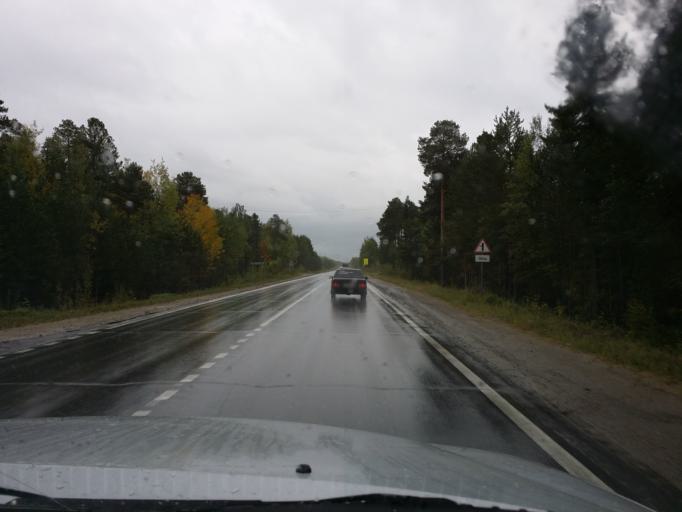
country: RU
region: Khanty-Mansiyskiy Avtonomnyy Okrug
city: Megion
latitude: 61.1543
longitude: 75.7382
